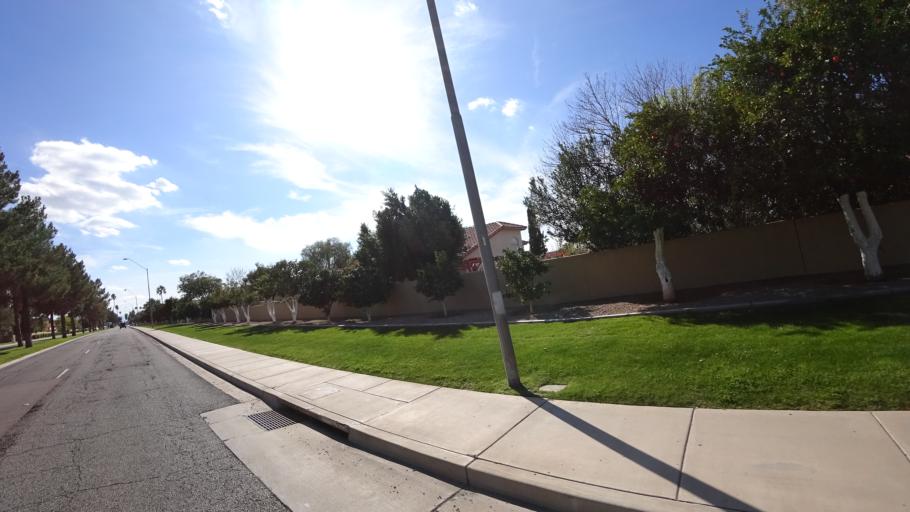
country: US
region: Arizona
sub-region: Maricopa County
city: Sun City
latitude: 33.6587
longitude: -112.2205
